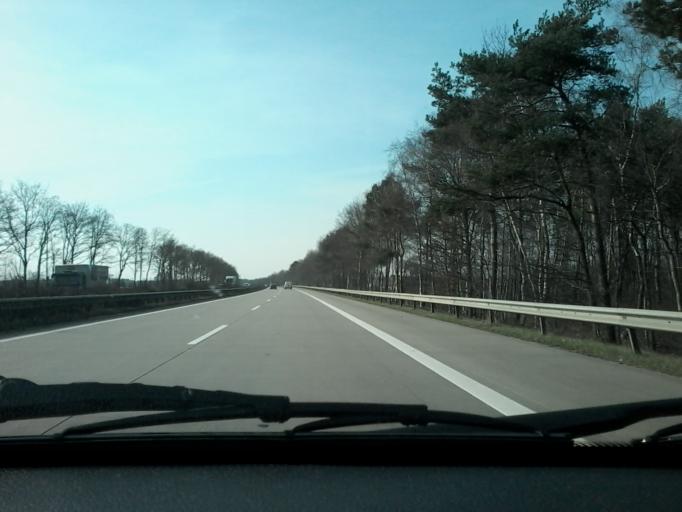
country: DE
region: Lower Saxony
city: Langwedel
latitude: 53.0113
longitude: 9.1448
